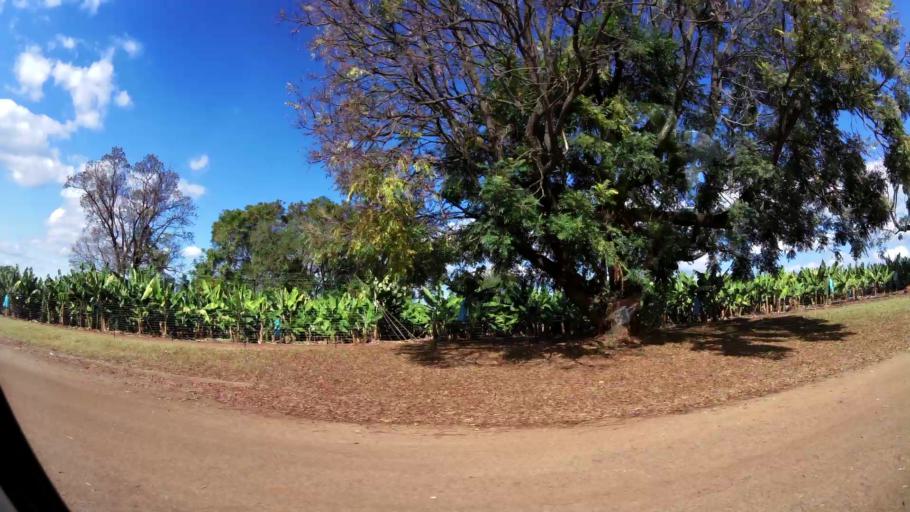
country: ZA
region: Limpopo
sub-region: Mopani District Municipality
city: Tzaneen
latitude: -23.8012
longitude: 30.1307
